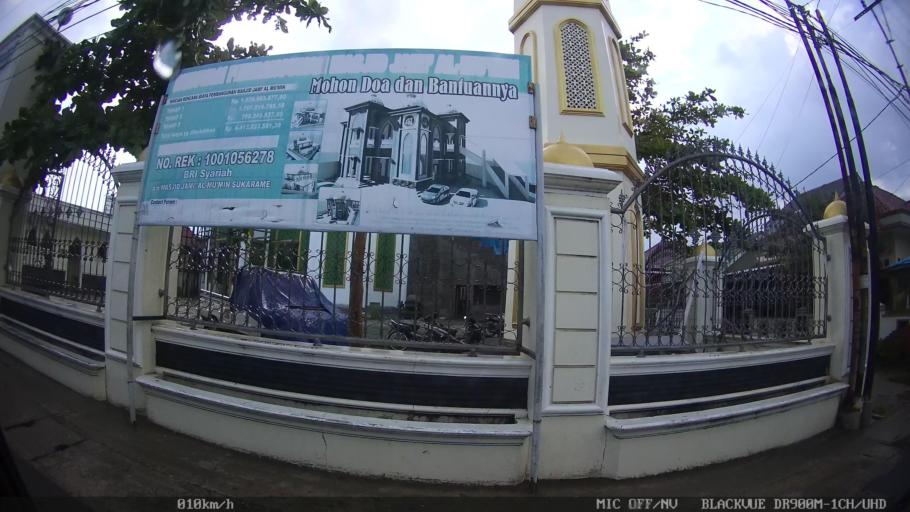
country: ID
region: Lampung
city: Kedaton
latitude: -5.3881
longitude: 105.2974
